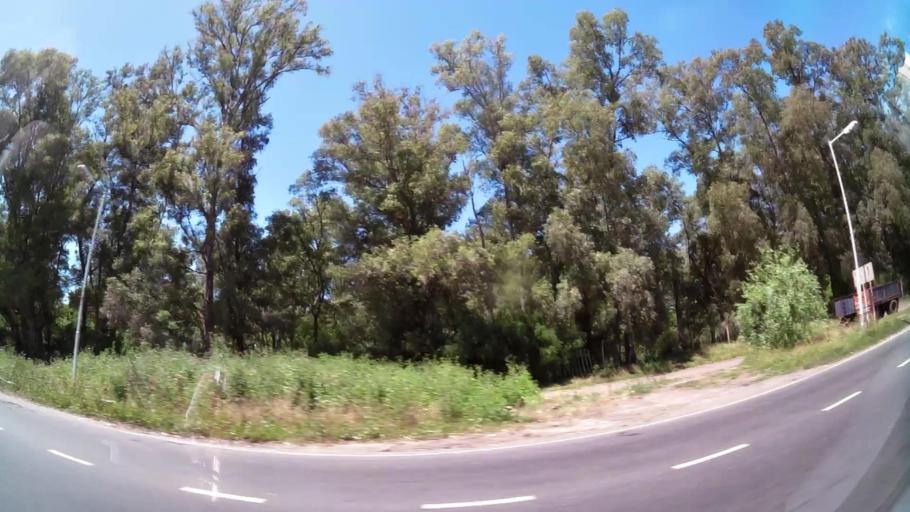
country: AR
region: Buenos Aires
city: Hurlingham
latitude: -34.5041
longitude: -58.6503
